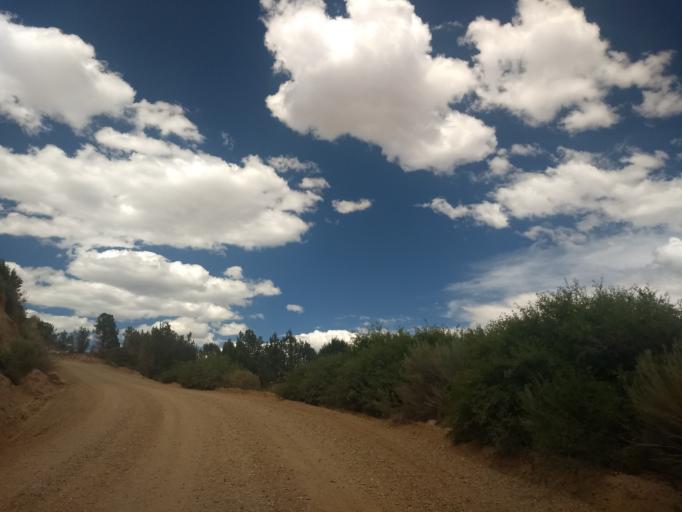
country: US
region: Utah
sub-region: Kane County
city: Kanab
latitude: 37.1462
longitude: -112.5398
